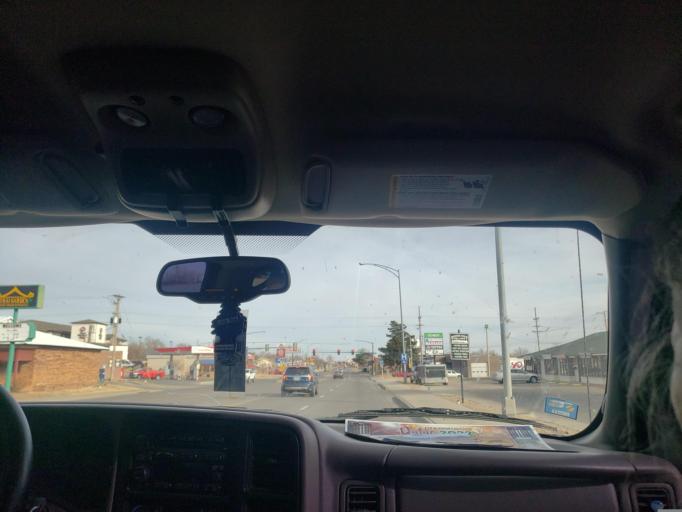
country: US
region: Kansas
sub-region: Ford County
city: Dodge City
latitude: 37.7537
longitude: -100.0344
